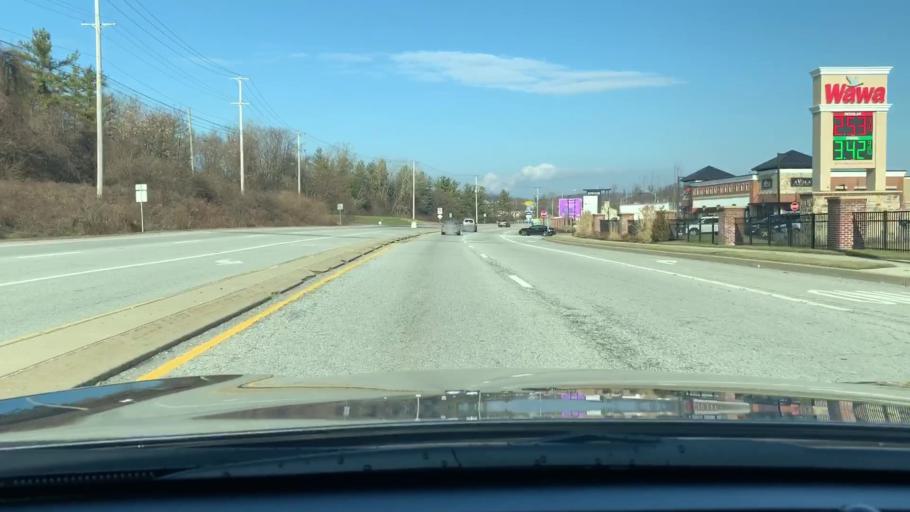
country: US
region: Pennsylvania
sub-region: Chester County
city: Malvern
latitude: 40.0669
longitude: -75.5364
